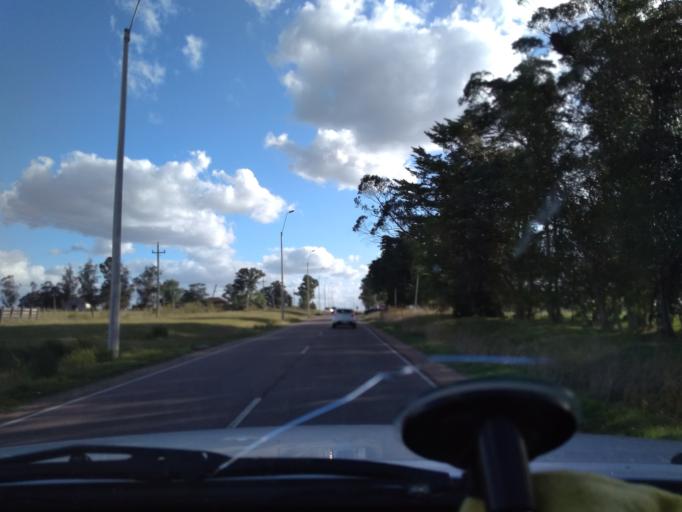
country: UY
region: Canelones
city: Tala
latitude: -34.3576
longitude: -55.7729
